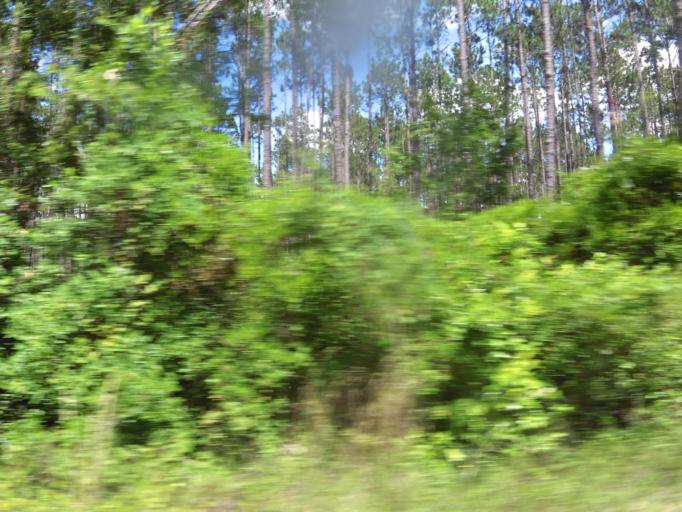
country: US
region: Florida
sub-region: Clay County
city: Asbury Lake
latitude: 29.8758
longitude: -81.8528
